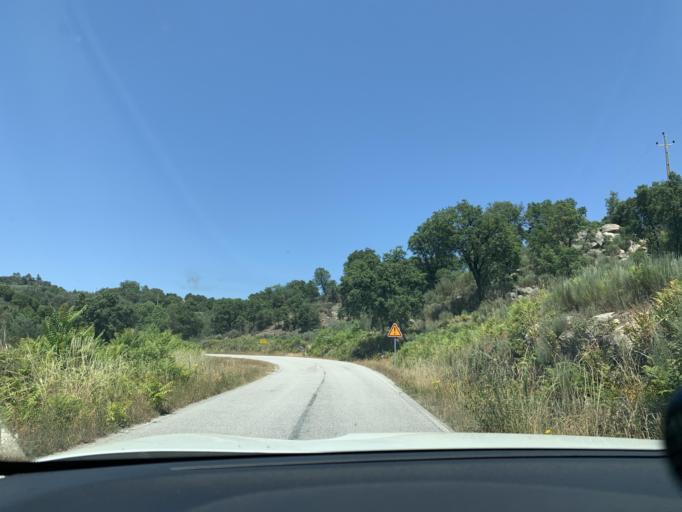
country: PT
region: Guarda
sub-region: Fornos de Algodres
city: Fornos de Algodres
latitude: 40.5743
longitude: -7.5945
